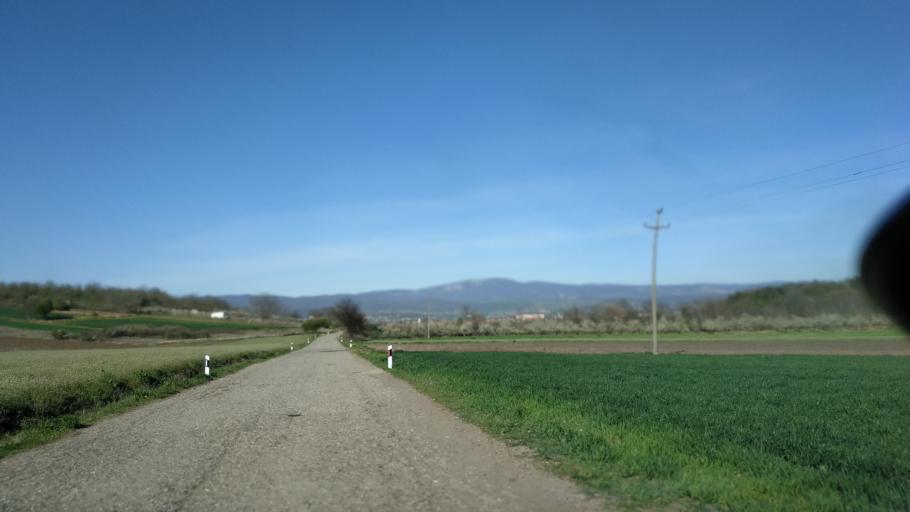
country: RS
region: Central Serbia
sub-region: Nisavski Okrug
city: Aleksinac
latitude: 43.4933
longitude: 21.6709
